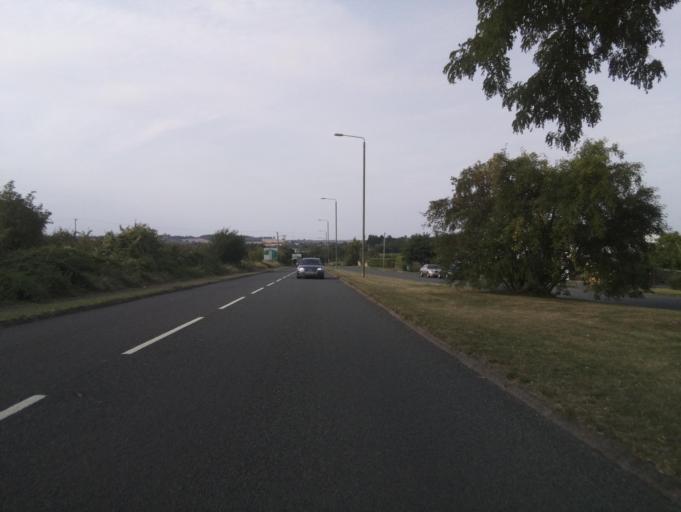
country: GB
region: England
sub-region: Worcestershire
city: Evesham
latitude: 52.1109
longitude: -1.9443
